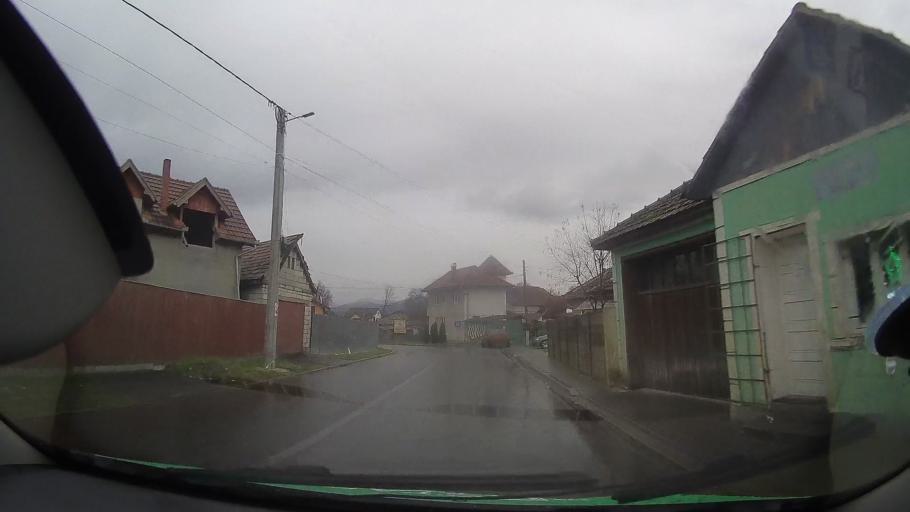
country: RO
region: Bihor
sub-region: Municipiul Beius
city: Beius
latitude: 46.6695
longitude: 22.3542
